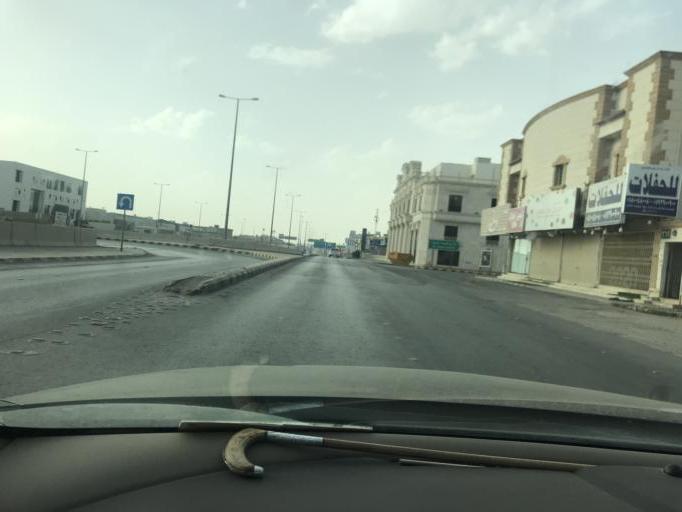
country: SA
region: Ar Riyad
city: Riyadh
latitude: 24.7800
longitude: 46.7072
